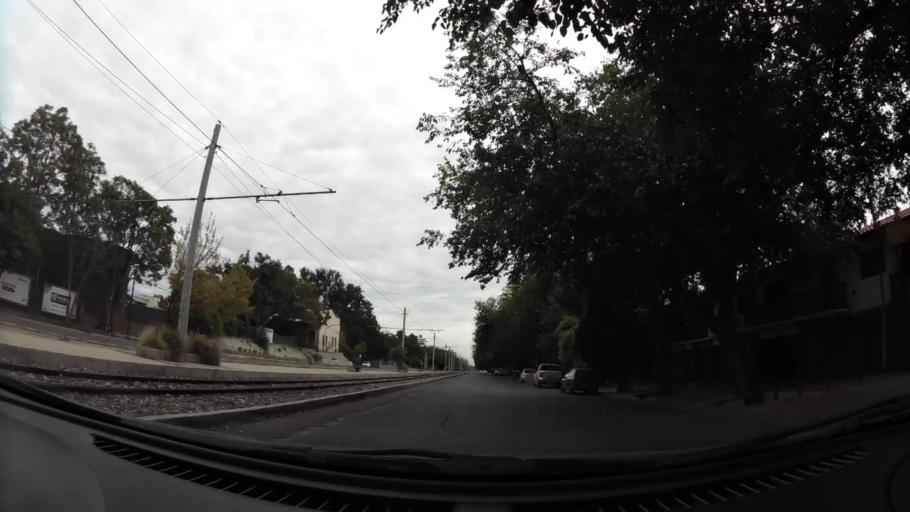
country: AR
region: Mendoza
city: Mendoza
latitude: -32.8948
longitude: -68.8512
